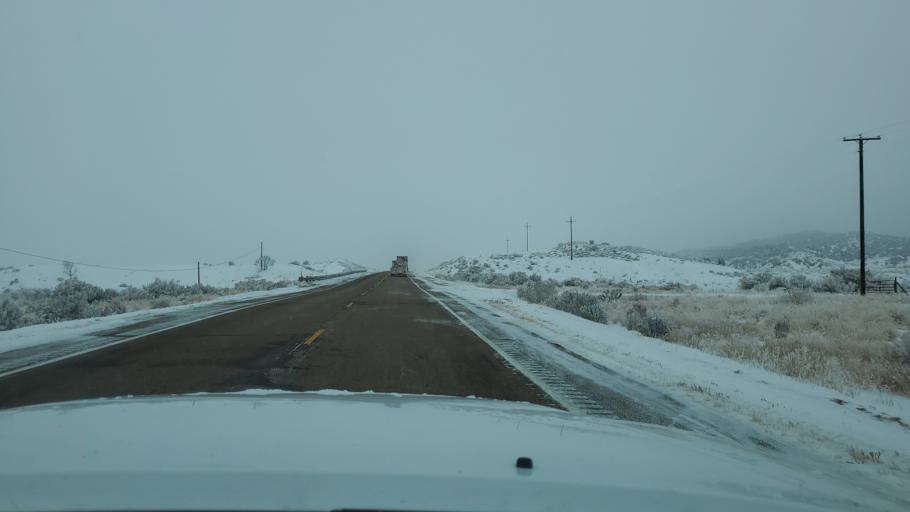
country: US
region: Colorado
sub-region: Rio Blanco County
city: Rangely
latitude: 40.2428
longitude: -108.9539
